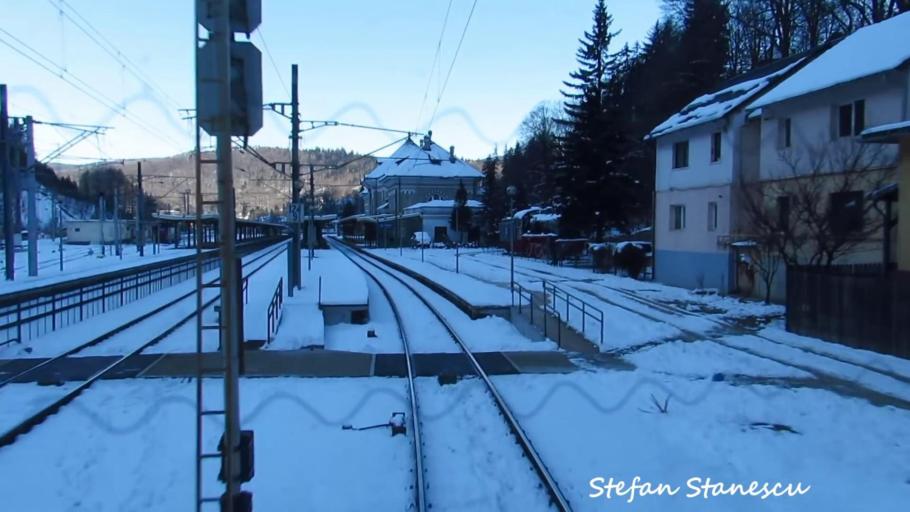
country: RO
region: Prahova
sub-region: Oras Sinaia
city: Sinaia
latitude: 45.3601
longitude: 25.5541
